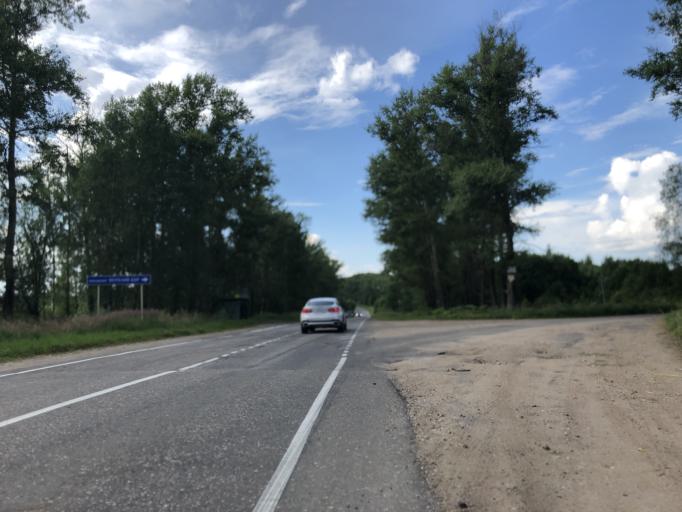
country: RU
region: Tverskaya
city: Rzhev
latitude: 56.2653
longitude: 34.2512
